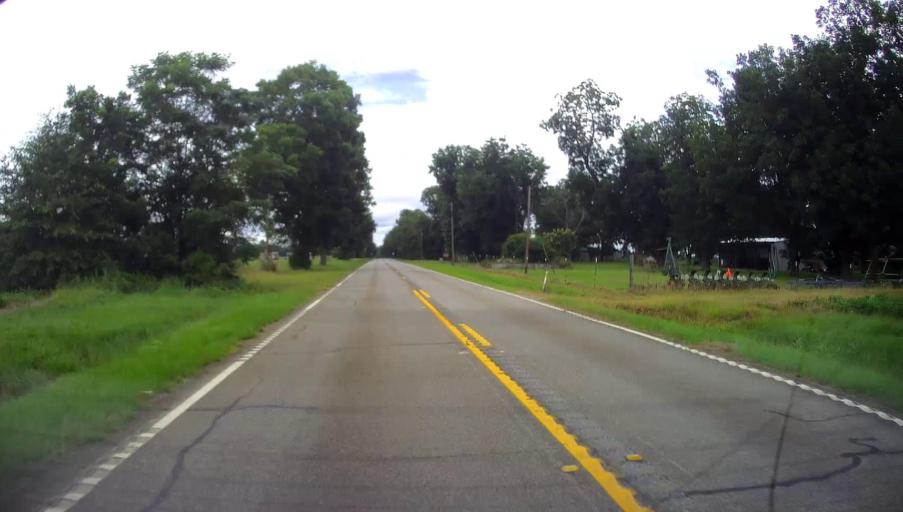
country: US
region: Georgia
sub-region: Schley County
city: Ellaville
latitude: 32.2250
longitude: -84.2802
